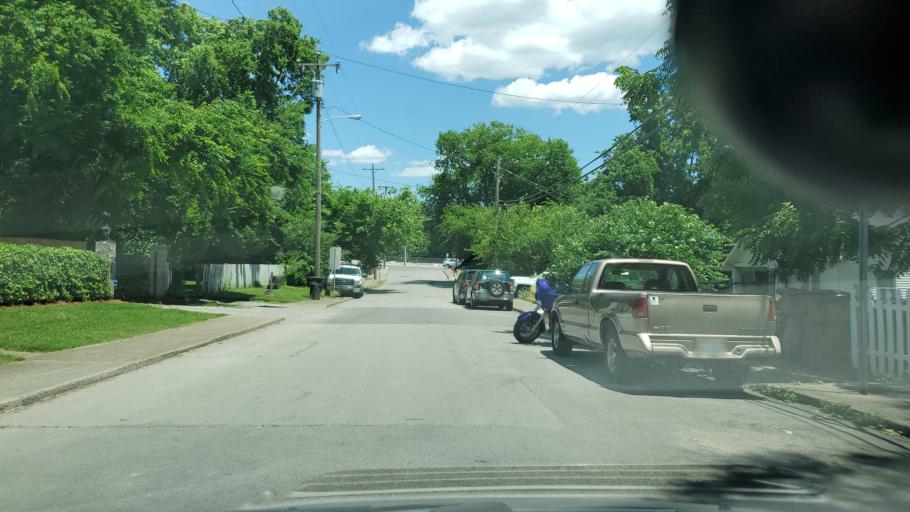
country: US
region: Tennessee
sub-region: Davidson County
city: Nashville
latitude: 36.1907
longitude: -86.7468
